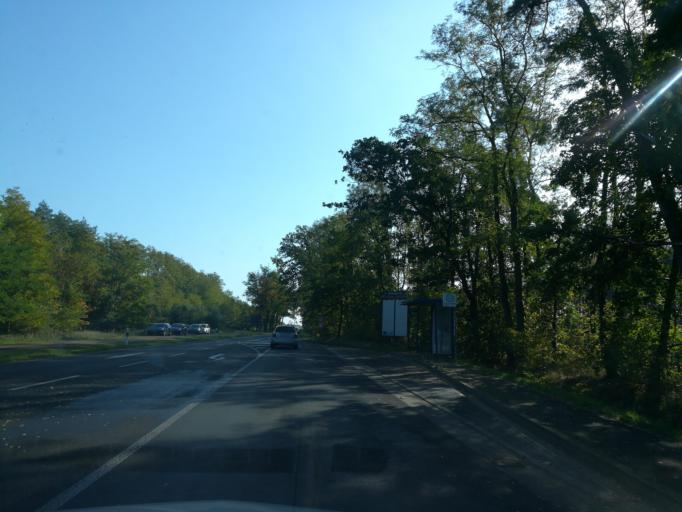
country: DE
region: Saxony-Anhalt
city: Gommern
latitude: 52.0893
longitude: 11.8018
